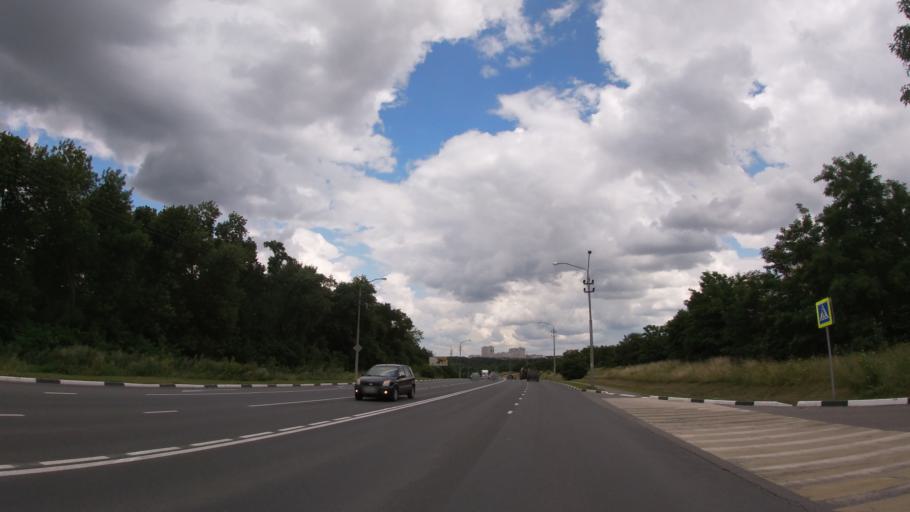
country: RU
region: Belgorod
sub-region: Belgorodskiy Rayon
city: Belgorod
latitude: 50.5538
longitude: 36.5811
